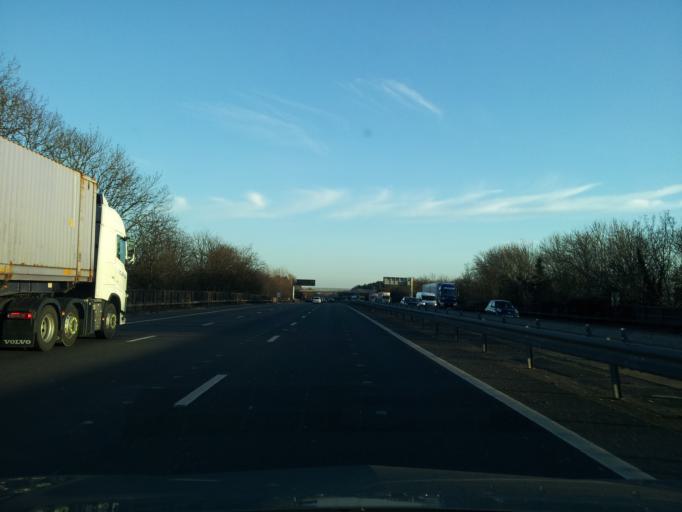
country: GB
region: England
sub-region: Milton Keynes
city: Newport Pagnell
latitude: 52.0808
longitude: -0.7441
